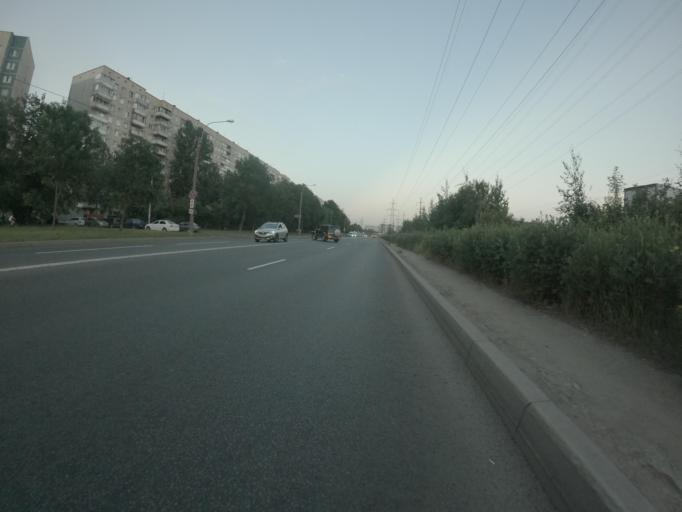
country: RU
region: St.-Petersburg
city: Krasnogvargeisky
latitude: 59.9410
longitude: 30.4662
